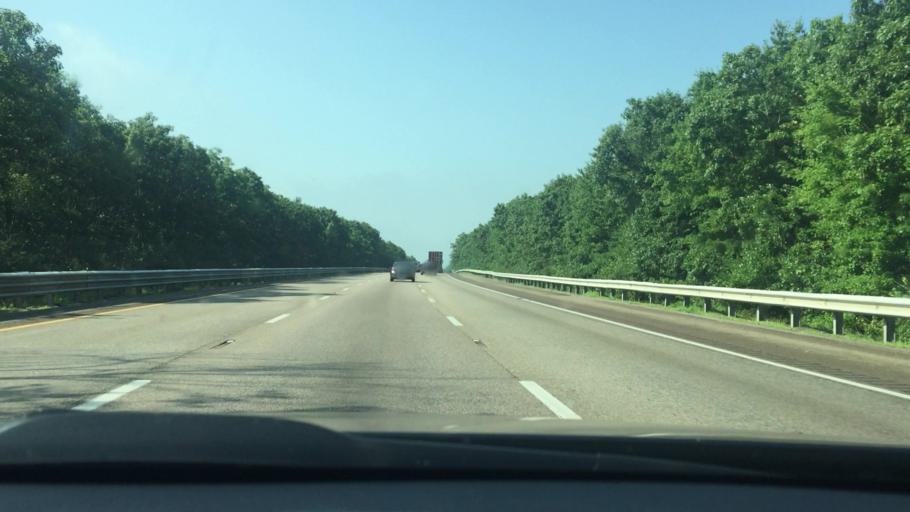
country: US
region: Massachusetts
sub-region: Norfolk County
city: Foxborough
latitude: 42.0785
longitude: -71.2232
